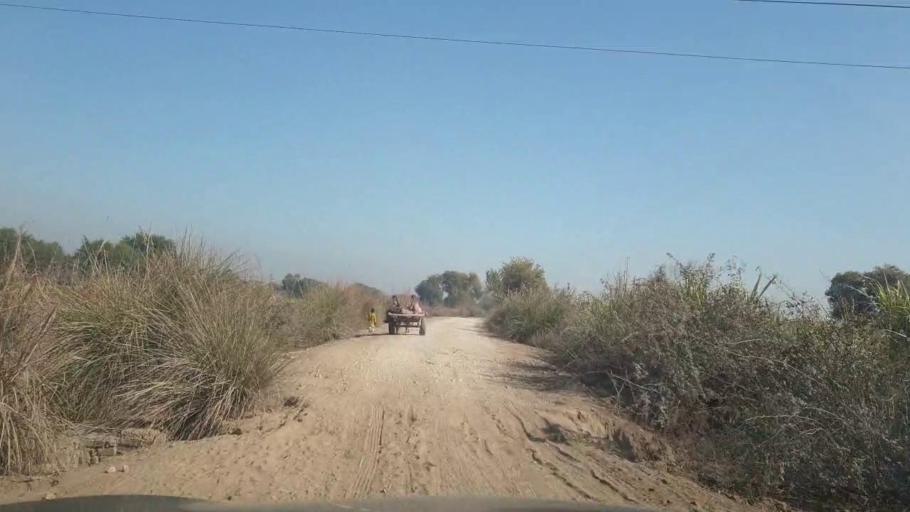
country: PK
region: Sindh
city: Mirpur Mathelo
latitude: 28.1276
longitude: 69.4974
